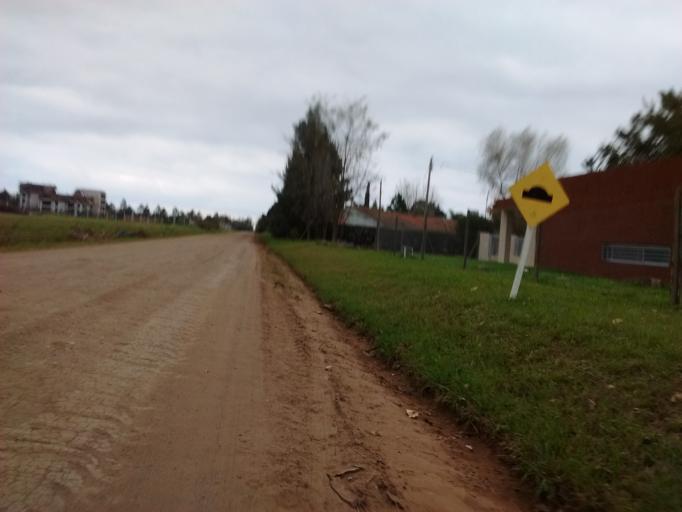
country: AR
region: Santa Fe
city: Funes
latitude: -32.9241
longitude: -60.8330
